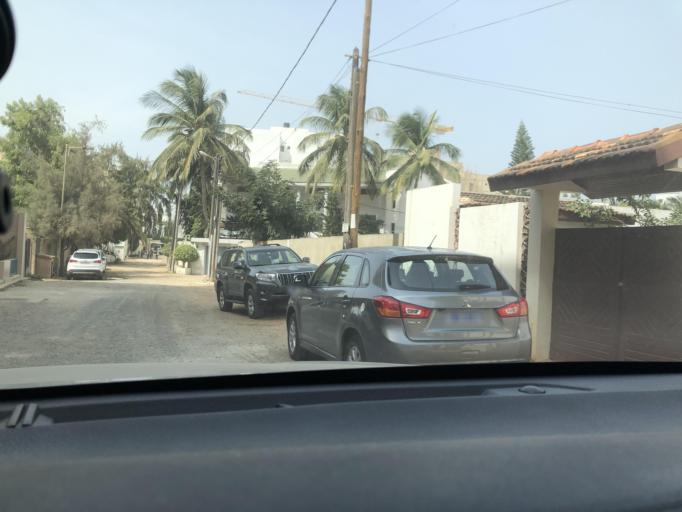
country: SN
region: Dakar
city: Mermoz Boabab
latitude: 14.7413
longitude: -17.5161
